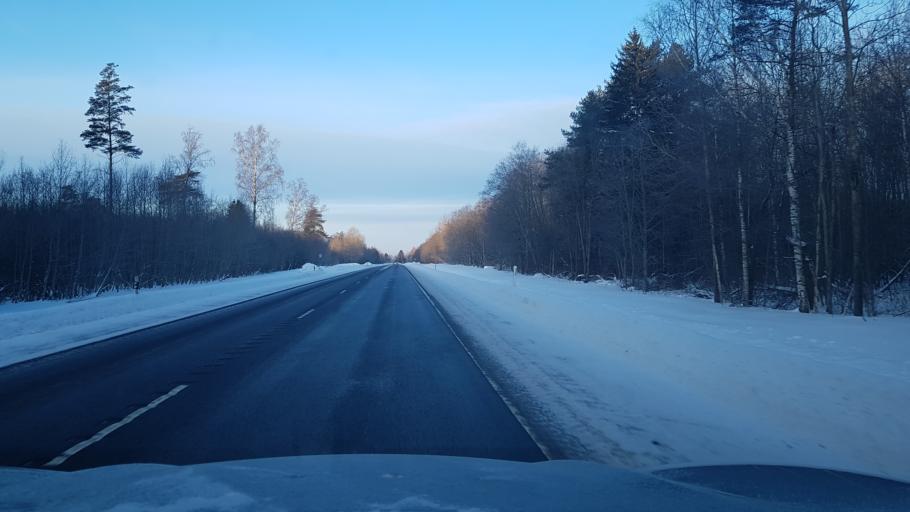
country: EE
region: Ida-Virumaa
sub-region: Toila vald
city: Voka
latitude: 59.3928
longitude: 27.6513
